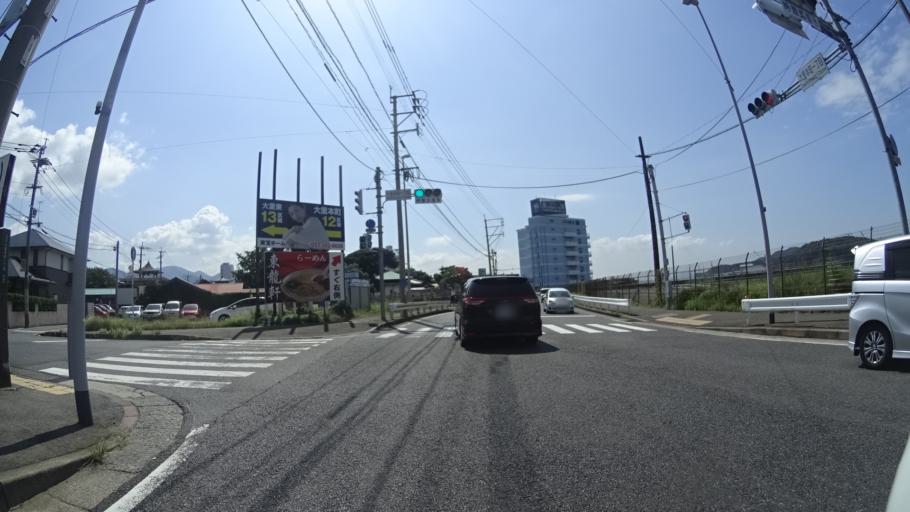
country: JP
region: Yamaguchi
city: Shimonoseki
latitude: 33.9128
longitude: 130.9358
